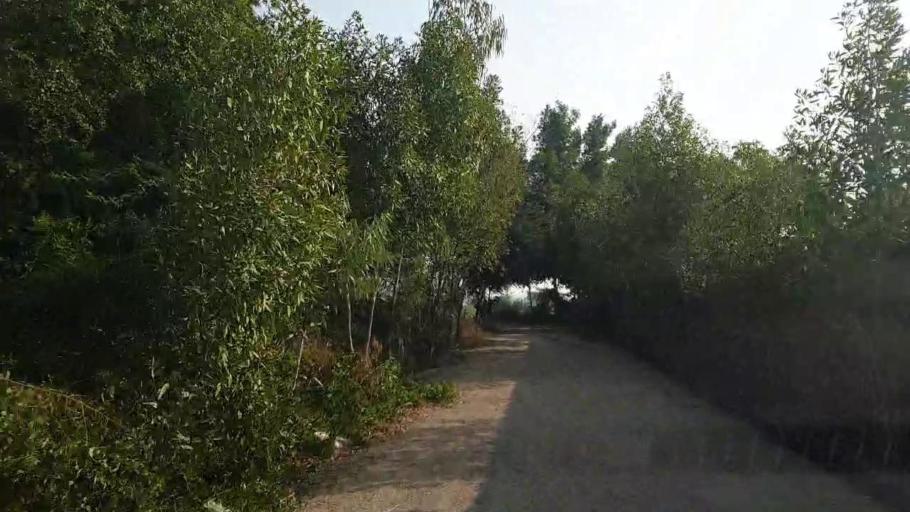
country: PK
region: Sindh
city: Kotri
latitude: 25.3575
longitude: 68.3219
